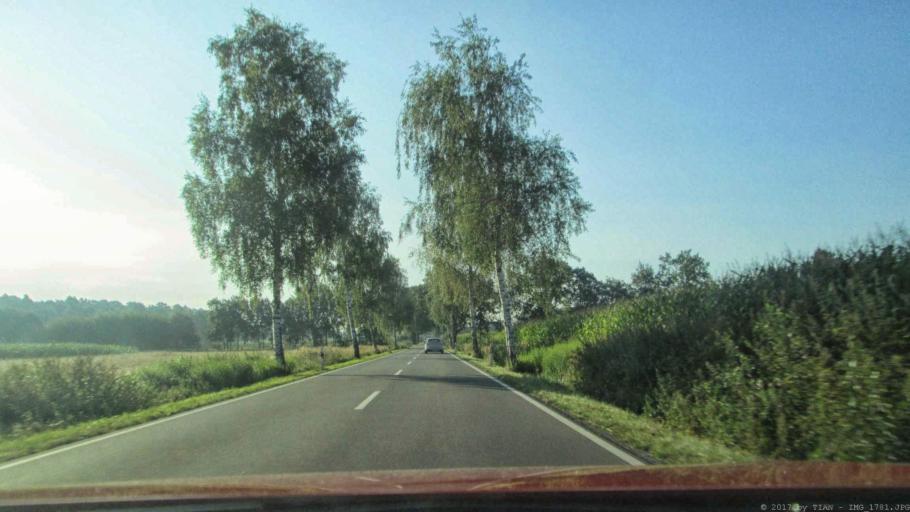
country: DE
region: Lower Saxony
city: Tiddische
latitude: 52.4890
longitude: 10.8084
